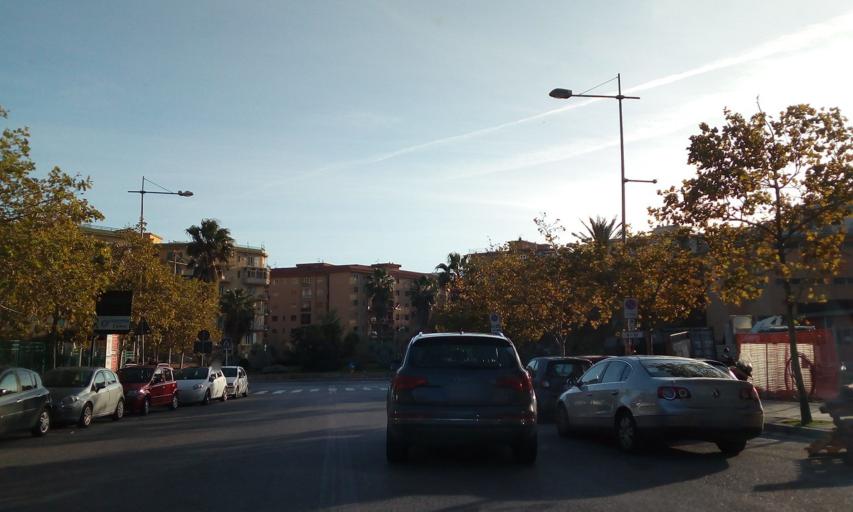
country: IT
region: Campania
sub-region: Provincia di Salerno
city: Capezzano Inferiore
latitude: 40.6849
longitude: 14.7750
